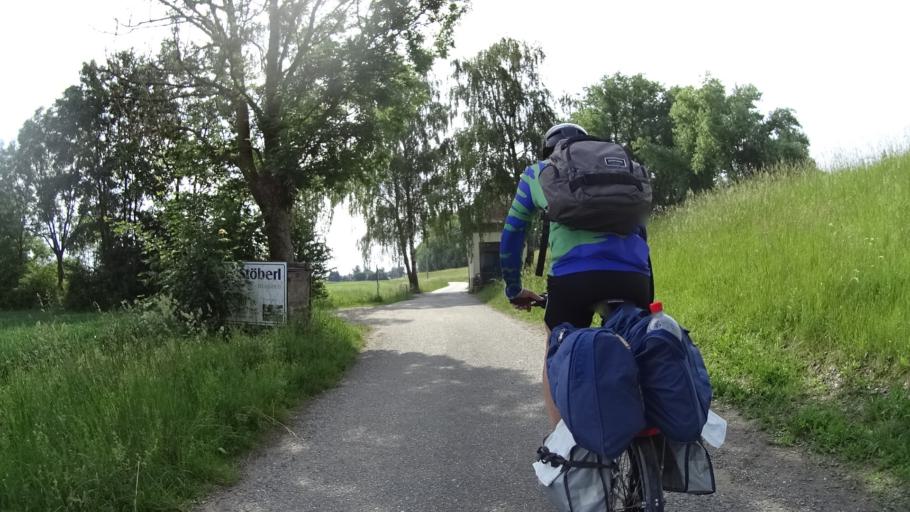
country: DE
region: Bavaria
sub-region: Lower Bavaria
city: Mariaposching
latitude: 48.8294
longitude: 12.7911
